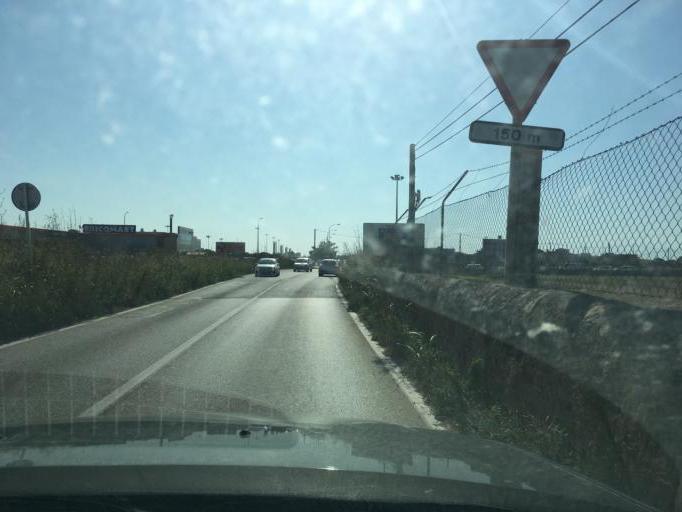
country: ES
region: Balearic Islands
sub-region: Illes Balears
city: Palma
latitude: 39.5754
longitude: 2.6852
